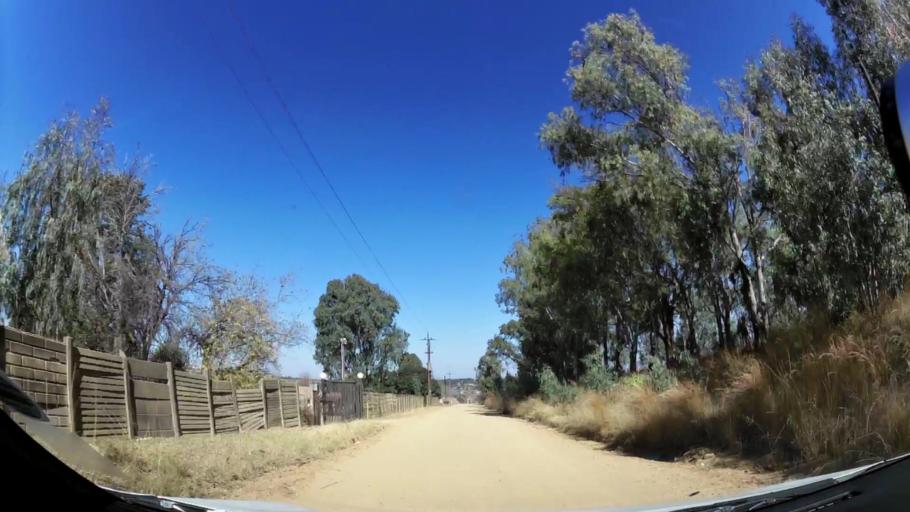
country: ZA
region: Gauteng
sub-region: City of Johannesburg Metropolitan Municipality
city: Midrand
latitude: -25.9401
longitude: 28.0859
